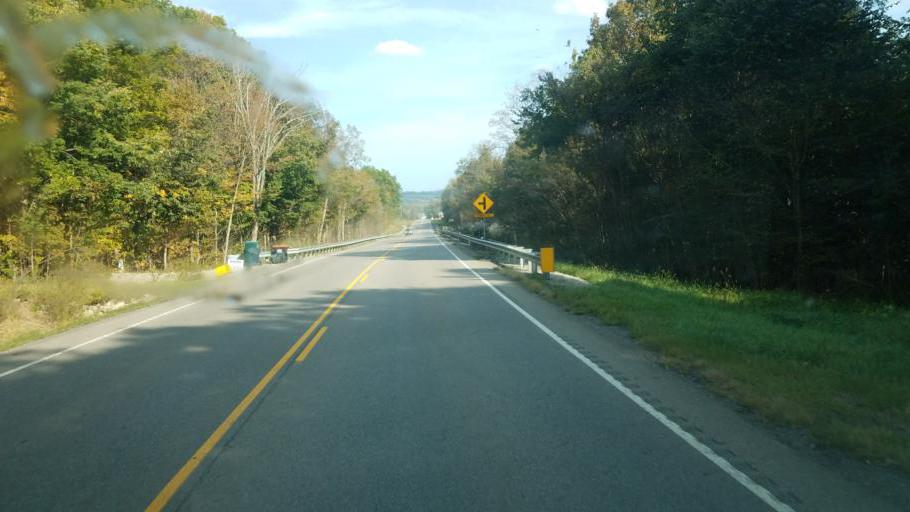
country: US
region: Ohio
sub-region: Licking County
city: Utica
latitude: 40.2319
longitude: -82.4702
